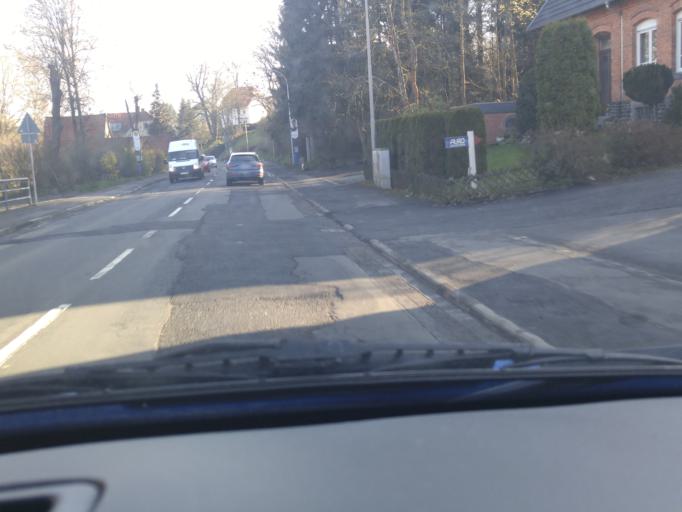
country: DE
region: Hesse
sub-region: Regierungsbezirk Giessen
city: Lauterbach
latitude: 50.6202
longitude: 9.3920
